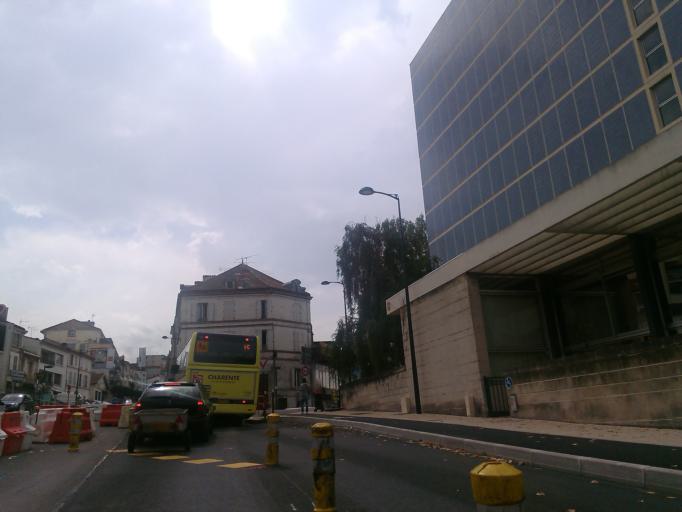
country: FR
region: Poitou-Charentes
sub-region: Departement de la Charente
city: Angouleme
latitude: 45.6522
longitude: 0.1633
